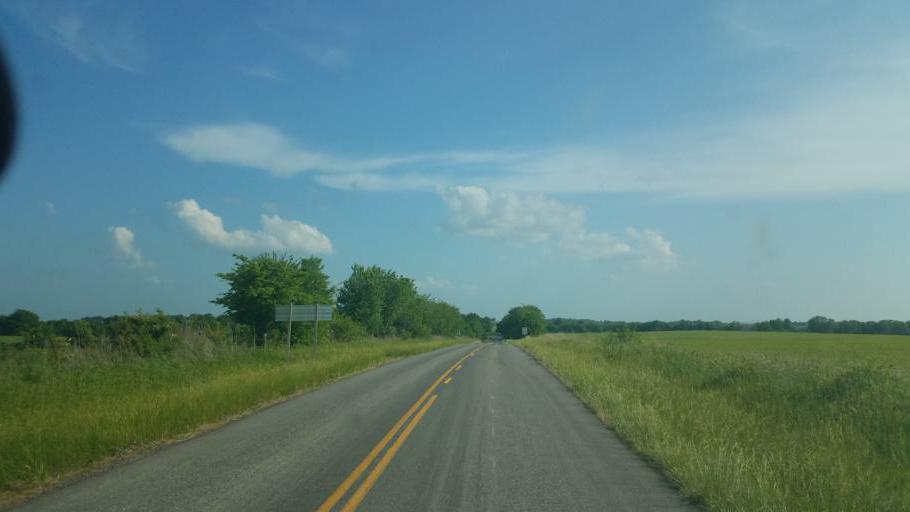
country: US
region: Missouri
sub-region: Moniteau County
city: California
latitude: 38.8110
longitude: -92.6047
